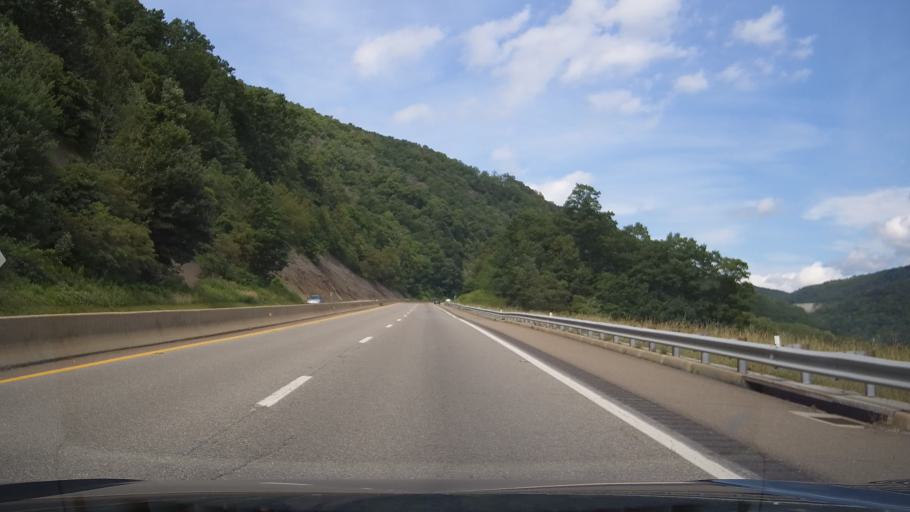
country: US
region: Virginia
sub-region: City of Norton
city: Norton
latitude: 36.9075
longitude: -82.6844
